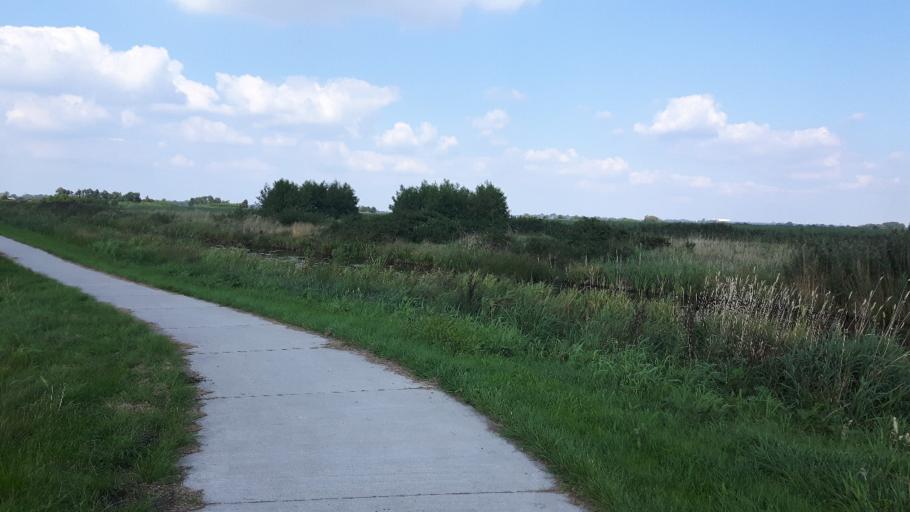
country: NL
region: Groningen
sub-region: Gemeente Leek
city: Leek
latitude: 53.1691
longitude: 6.4254
